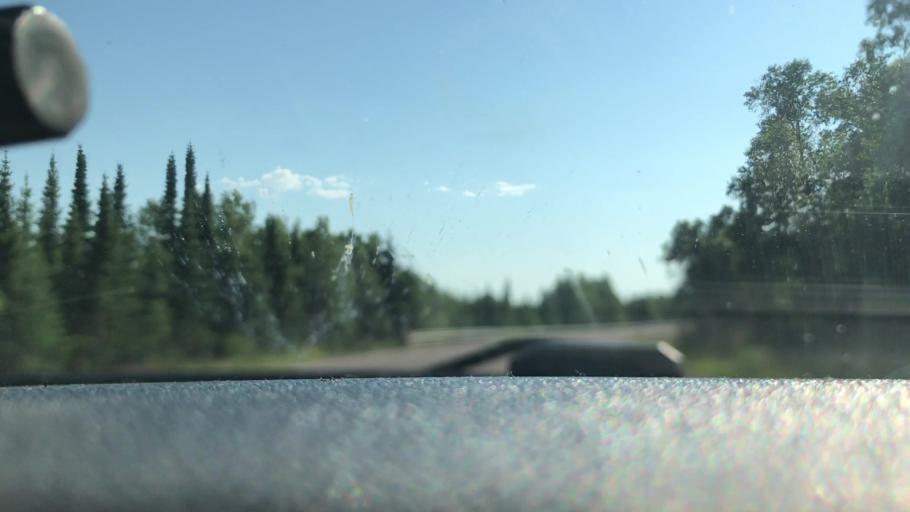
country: US
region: Minnesota
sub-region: Cook County
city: Grand Marais
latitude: 47.8323
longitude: -89.9764
